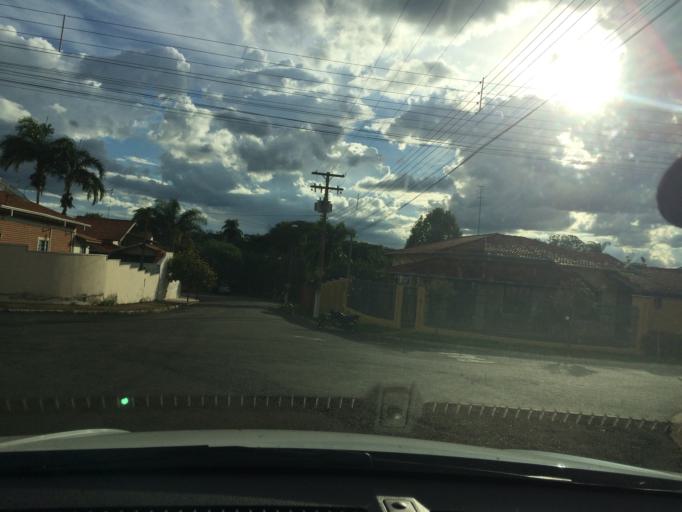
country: BR
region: Sao Paulo
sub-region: Casa Branca
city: Casa Branca
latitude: -21.7809
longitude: -47.0841
